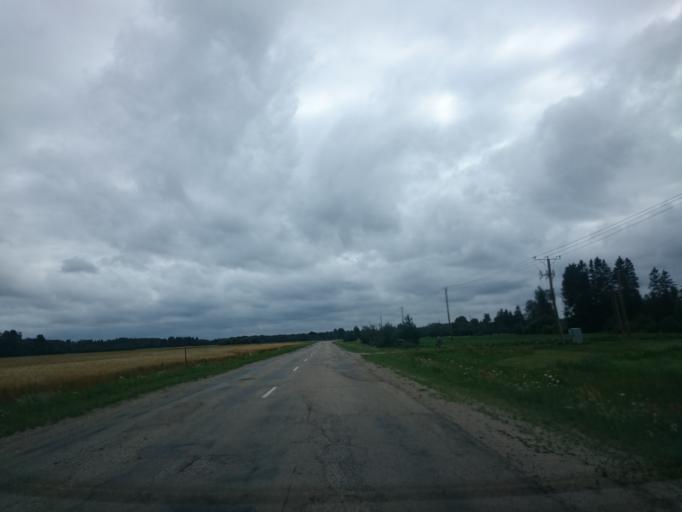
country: LV
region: Pavilostas
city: Pavilosta
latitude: 56.8215
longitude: 21.2270
